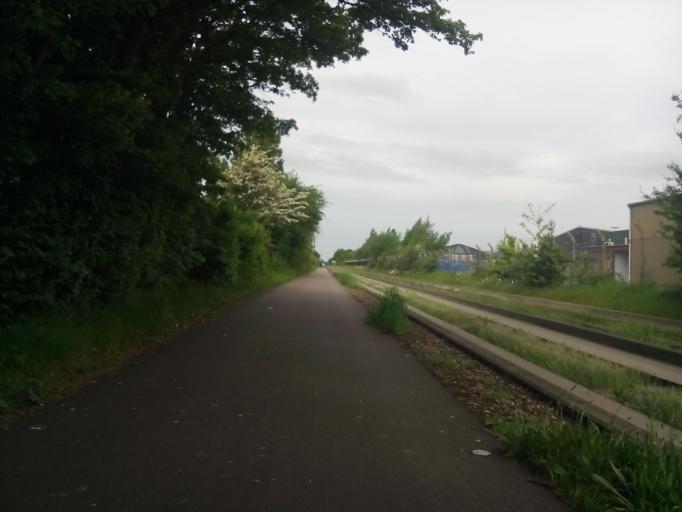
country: GB
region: England
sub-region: Cambridgeshire
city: Histon
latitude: 52.2469
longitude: 0.1023
